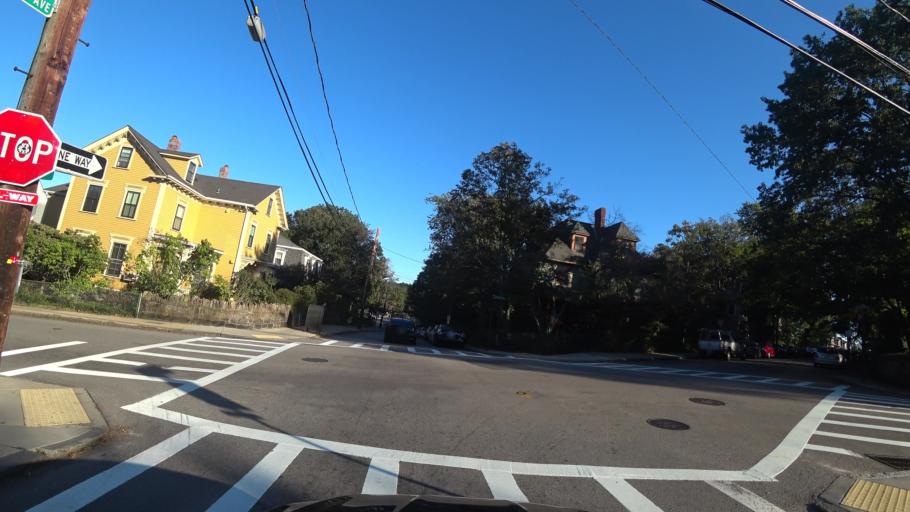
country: US
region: Massachusetts
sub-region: Suffolk County
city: Jamaica Plain
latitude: 42.3108
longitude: -71.1092
